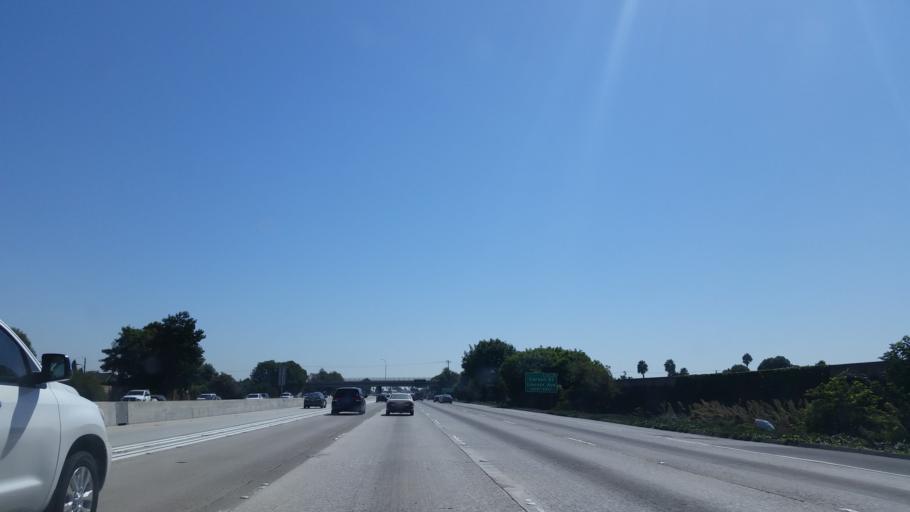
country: US
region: California
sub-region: Los Angeles County
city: Hawaiian Gardens
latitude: 33.8415
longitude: -118.0901
